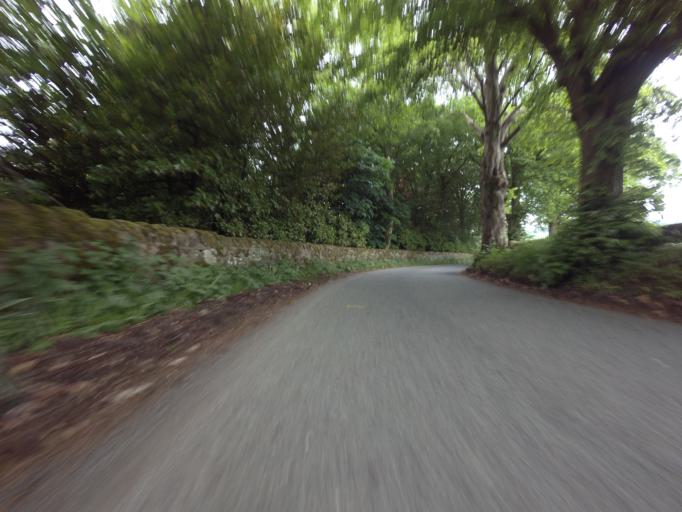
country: GB
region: Scotland
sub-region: Perth and Kinross
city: Kinross
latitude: 56.1636
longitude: -3.4488
